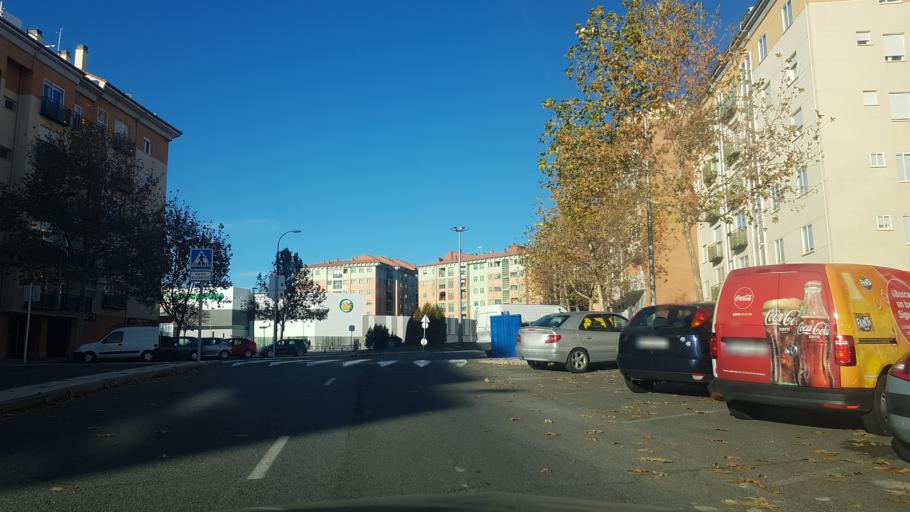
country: ES
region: Castille and Leon
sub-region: Provincia de Avila
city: Avila
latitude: 40.6481
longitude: -4.6775
